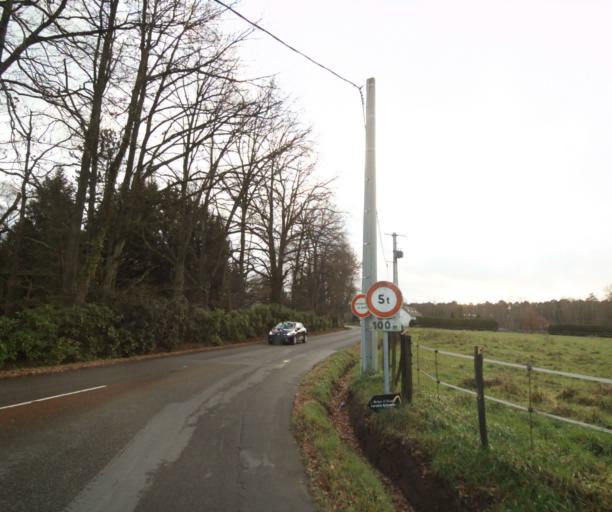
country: FR
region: Pays de la Loire
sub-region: Departement de la Sarthe
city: Ruaudin
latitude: 47.9633
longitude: 0.2427
